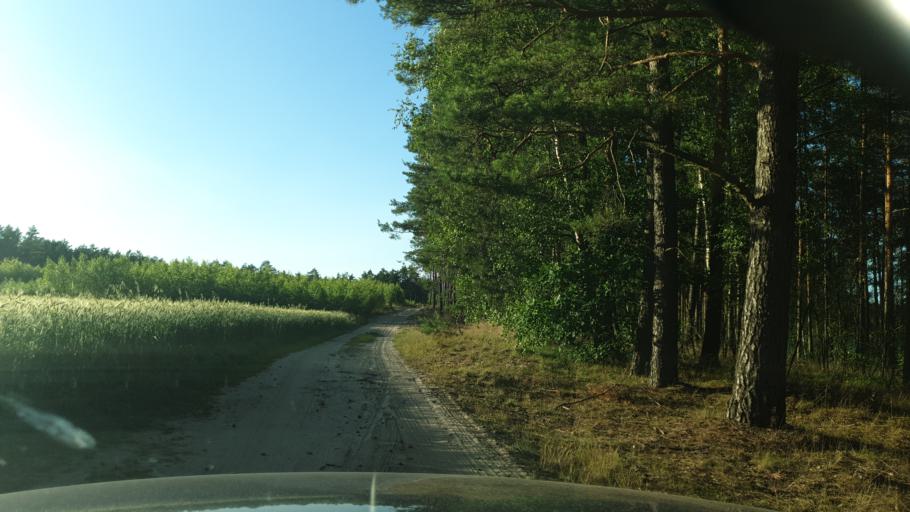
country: PL
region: Pomeranian Voivodeship
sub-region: Powiat bytowski
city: Lipnica
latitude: 53.8825
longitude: 17.4268
